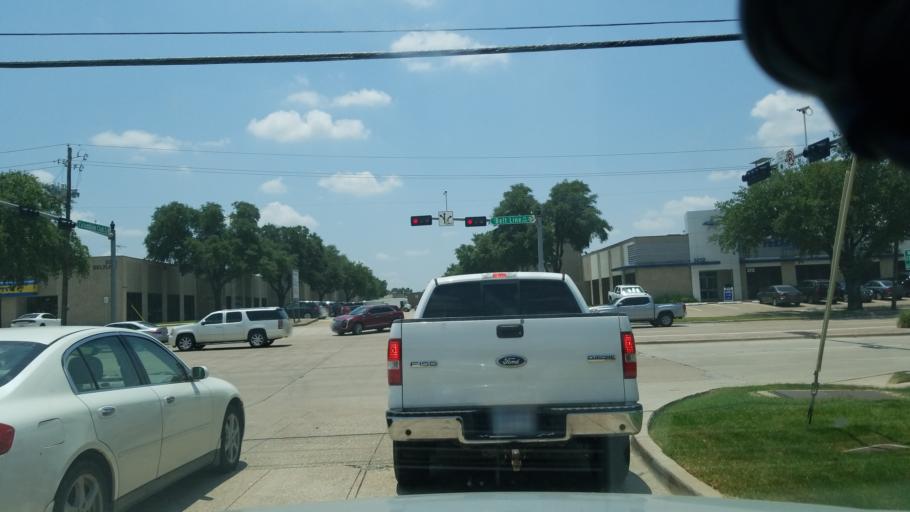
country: US
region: Texas
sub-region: Dallas County
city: Carrollton
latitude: 32.9536
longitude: -96.8686
